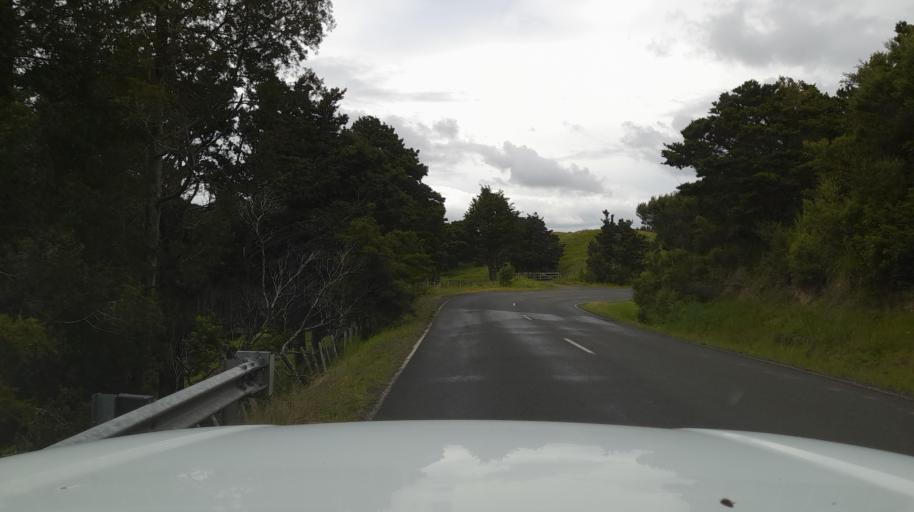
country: NZ
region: Northland
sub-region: Far North District
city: Kaitaia
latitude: -35.2817
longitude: 173.3733
